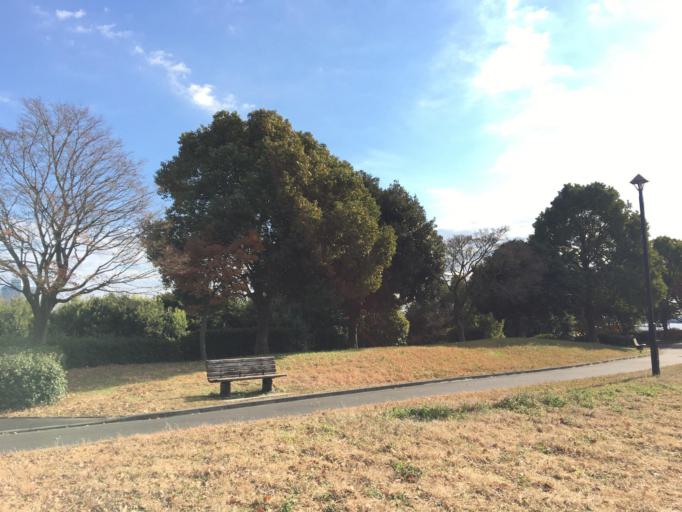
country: JP
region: Tokyo
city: Urayasu
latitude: 35.6860
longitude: 139.8483
